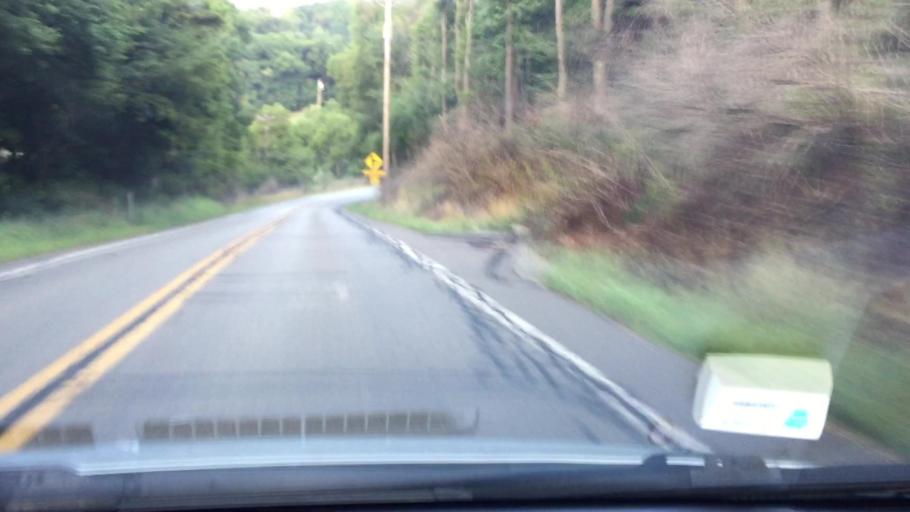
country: US
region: Pennsylvania
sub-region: Allegheny County
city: Gibsonia
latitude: 40.6315
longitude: -79.9900
